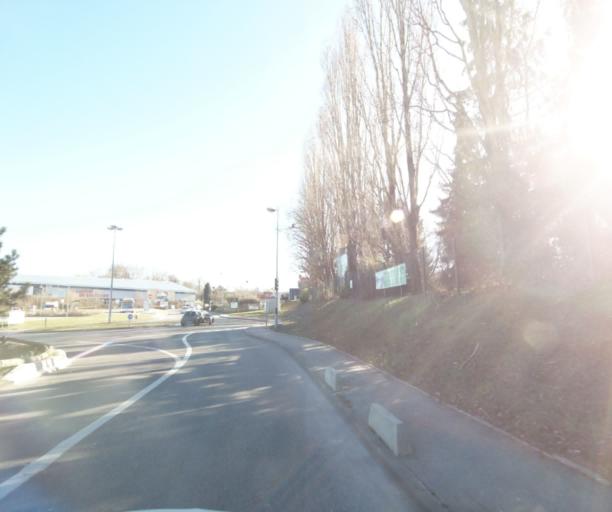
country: FR
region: Lorraine
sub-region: Departement de Meurthe-et-Moselle
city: Vandoeuvre-les-Nancy
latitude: 48.6382
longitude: 6.1845
